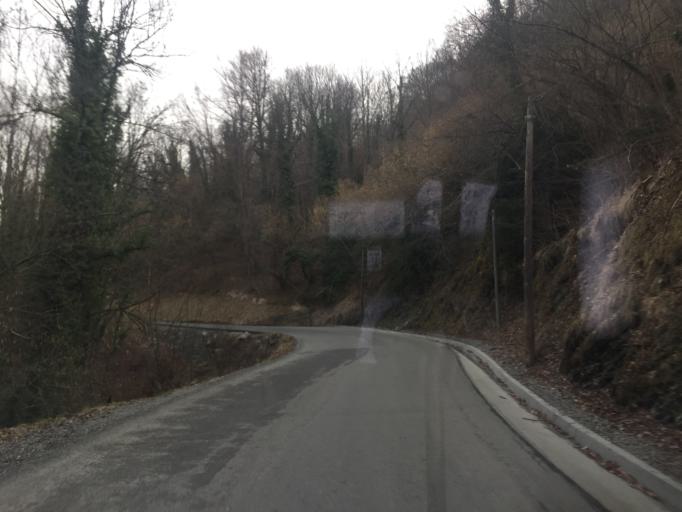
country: FR
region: Midi-Pyrenees
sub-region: Departement des Hautes-Pyrenees
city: Saint-Lary-Soulan
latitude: 42.8140
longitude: 0.3261
